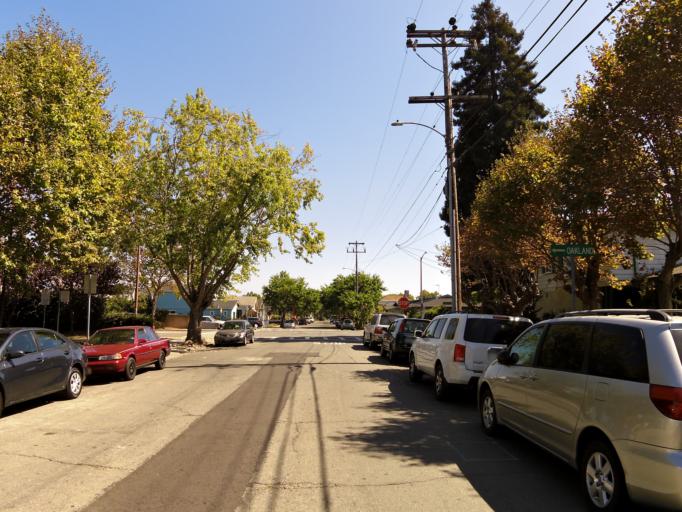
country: US
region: California
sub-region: Alameda County
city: Oakland
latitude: 37.7782
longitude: -122.2751
